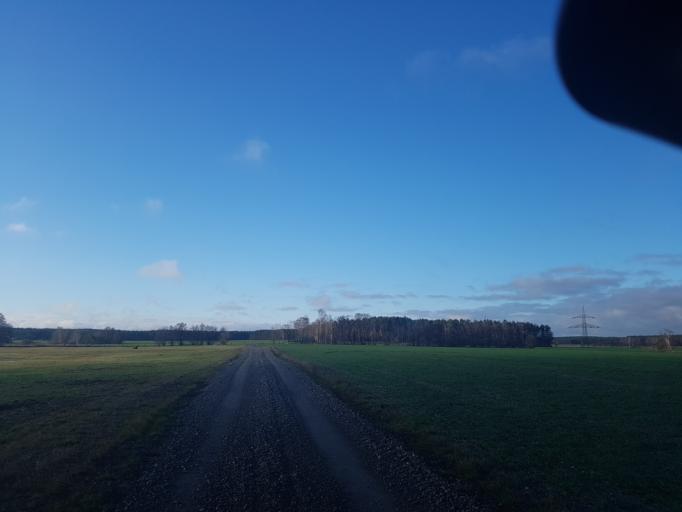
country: DE
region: Brandenburg
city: Schonborn
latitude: 51.5531
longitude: 13.4702
